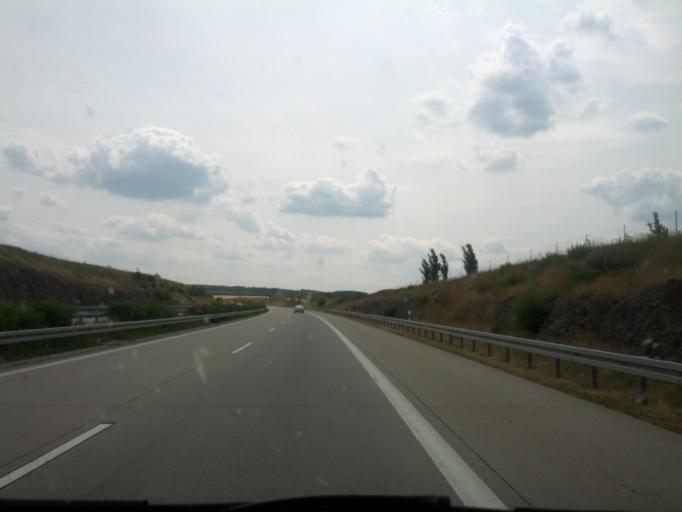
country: DE
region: Saxony
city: Liebstadt
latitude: 50.8117
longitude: 13.8823
